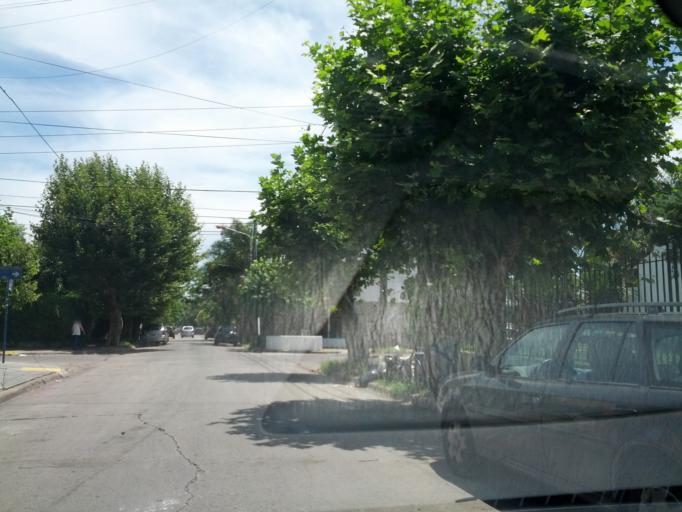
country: AR
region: Buenos Aires
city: San Justo
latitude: -34.6454
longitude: -58.5740
